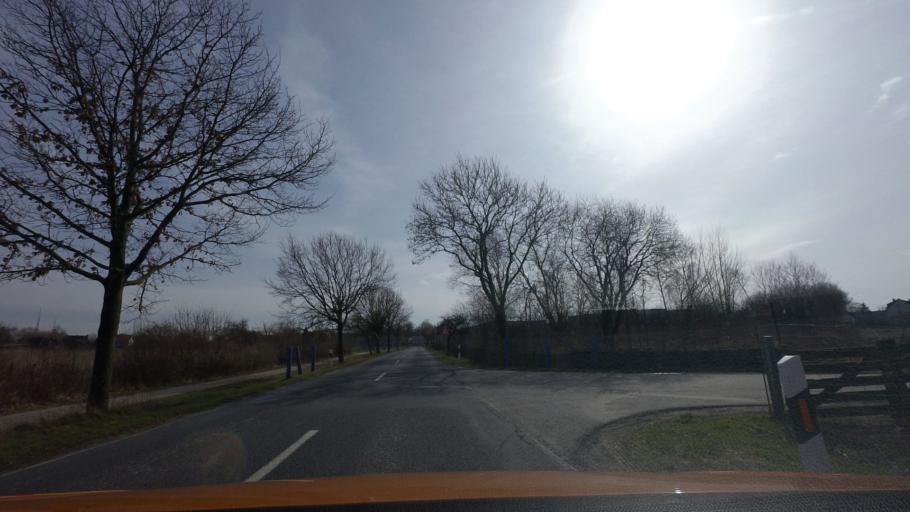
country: DE
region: Lower Saxony
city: Ronnenberg
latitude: 52.3232
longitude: 9.6456
